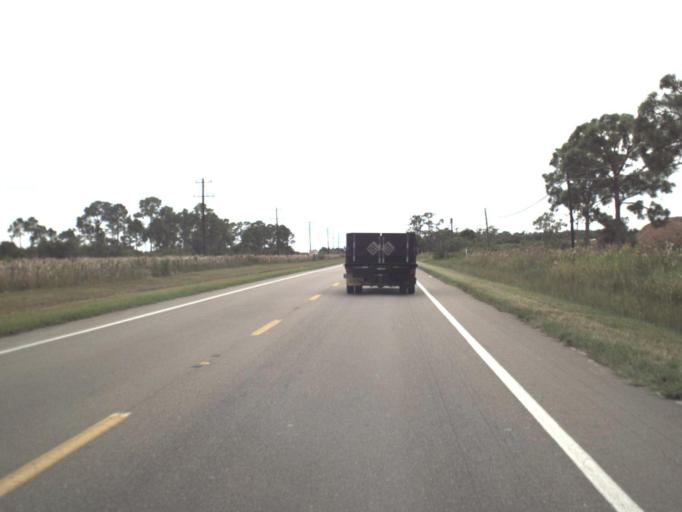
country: US
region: Florida
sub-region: Lee County
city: Fort Myers Shores
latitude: 26.7770
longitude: -81.7607
